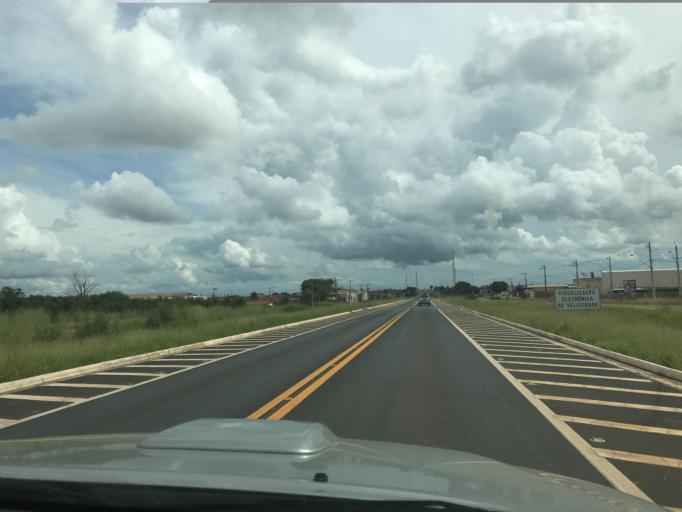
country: BR
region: Minas Gerais
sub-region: Patrocinio
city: Patrocinio
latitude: -19.1017
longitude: -46.6766
